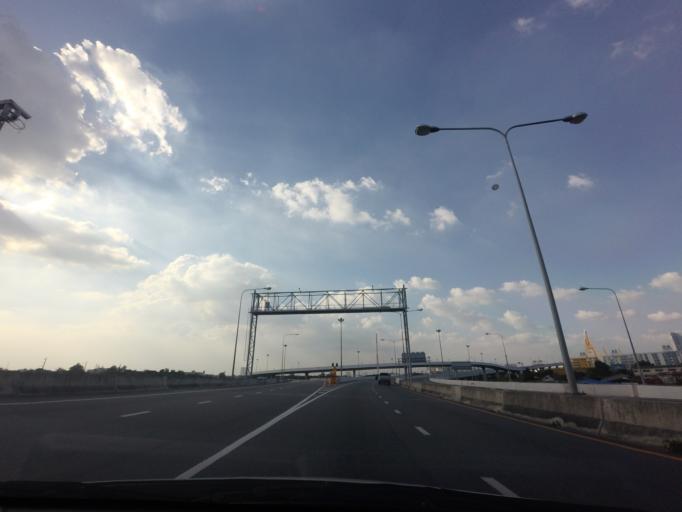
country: TH
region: Samut Prakan
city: Phra Pradaeng
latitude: 13.6451
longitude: 100.5432
